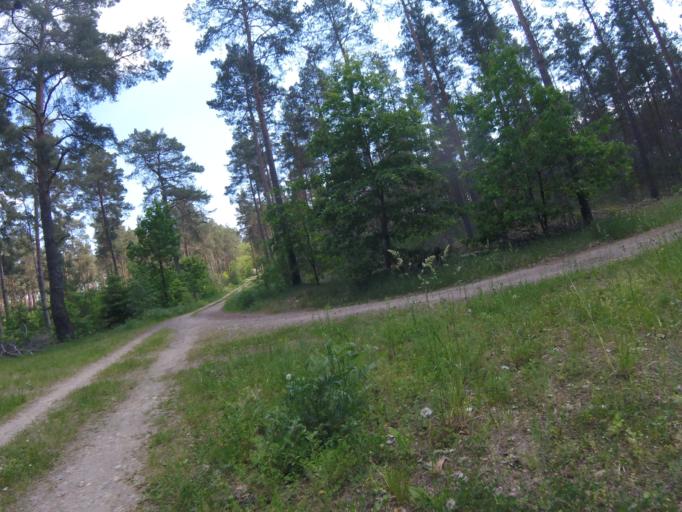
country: DE
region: Brandenburg
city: Teupitz
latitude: 52.1015
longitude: 13.6065
